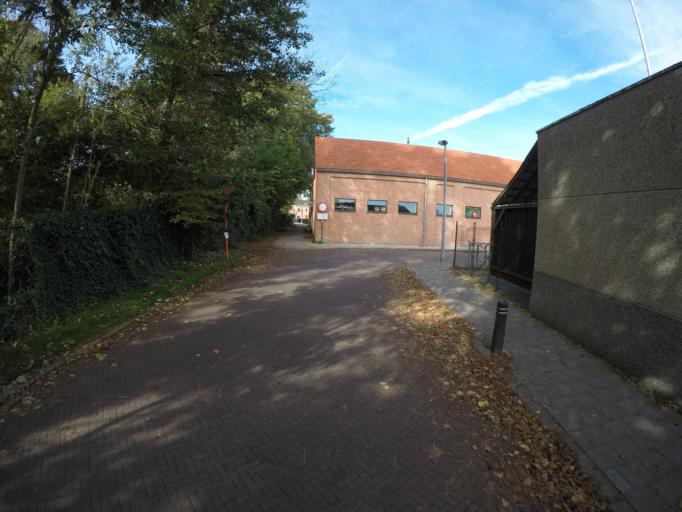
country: BE
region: Flanders
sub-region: Provincie Oost-Vlaanderen
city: Stekene
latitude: 51.1563
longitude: 4.0465
